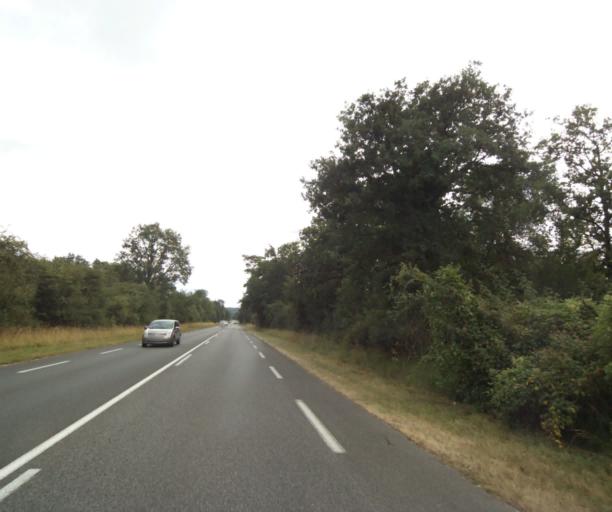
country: FR
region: Ile-de-France
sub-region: Departement de Seine-et-Marne
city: Bois-le-Roi
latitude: 48.4475
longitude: 2.6882
